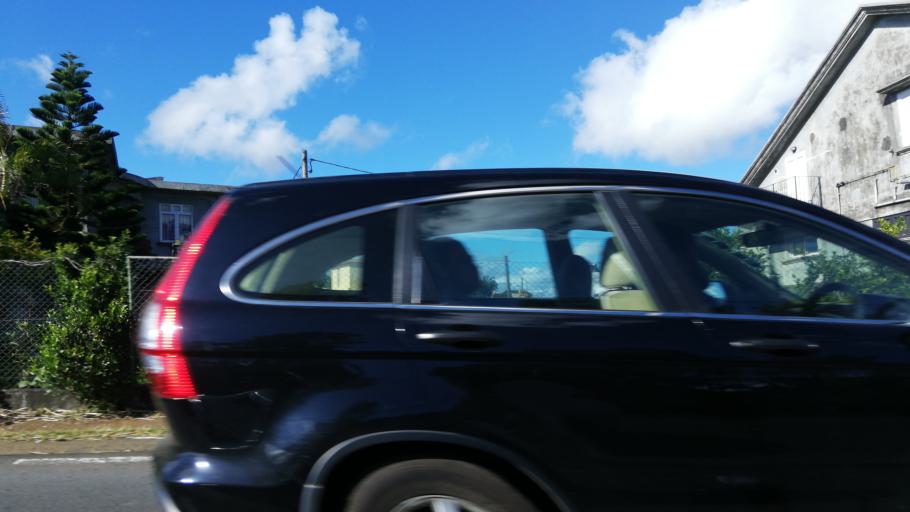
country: MU
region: Moka
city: La Dagotiere
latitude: -20.2328
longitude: 57.5554
